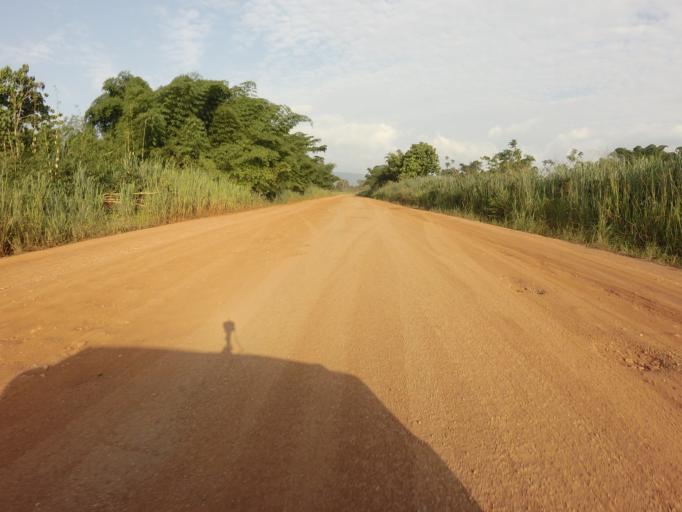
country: GH
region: Volta
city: Kpandu
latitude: 6.9879
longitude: 0.4432
